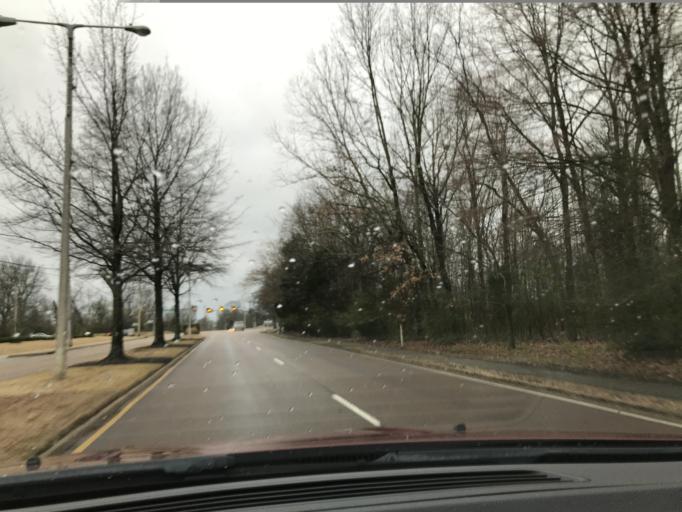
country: US
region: Tennessee
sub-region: Shelby County
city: Collierville
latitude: 35.0553
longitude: -89.6862
